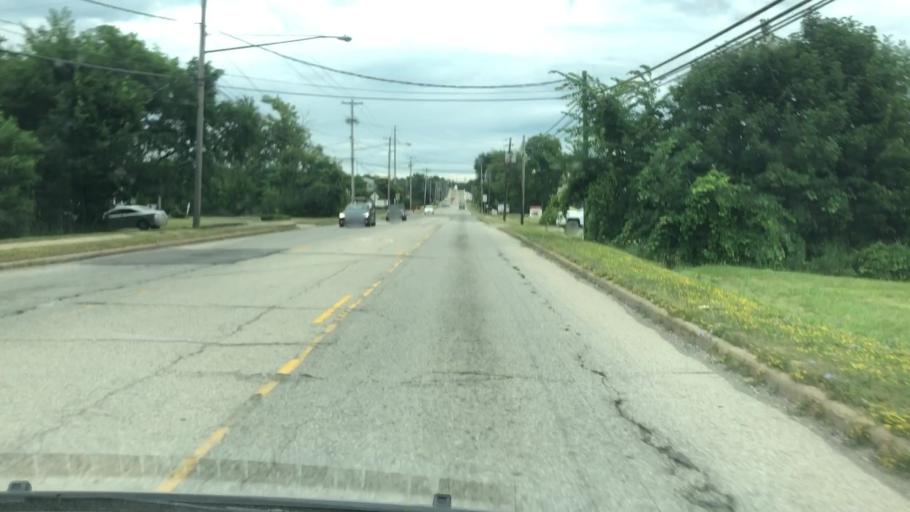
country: US
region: Ohio
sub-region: Summit County
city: Macedonia
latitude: 41.2990
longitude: -81.5072
